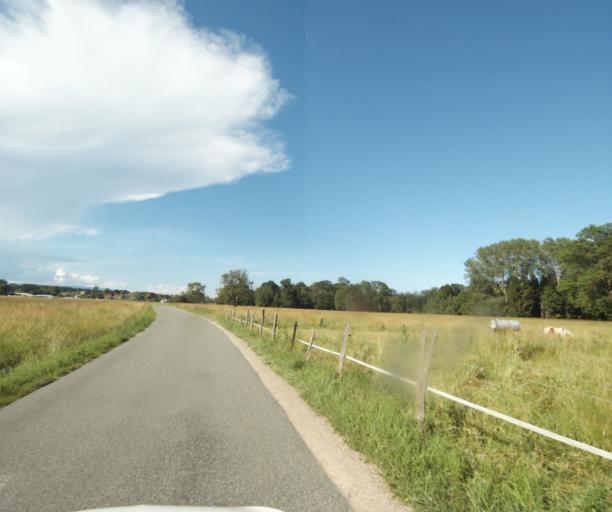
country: FR
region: Rhone-Alpes
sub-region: Departement de la Haute-Savoie
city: Massongy
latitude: 46.3410
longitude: 6.3283
